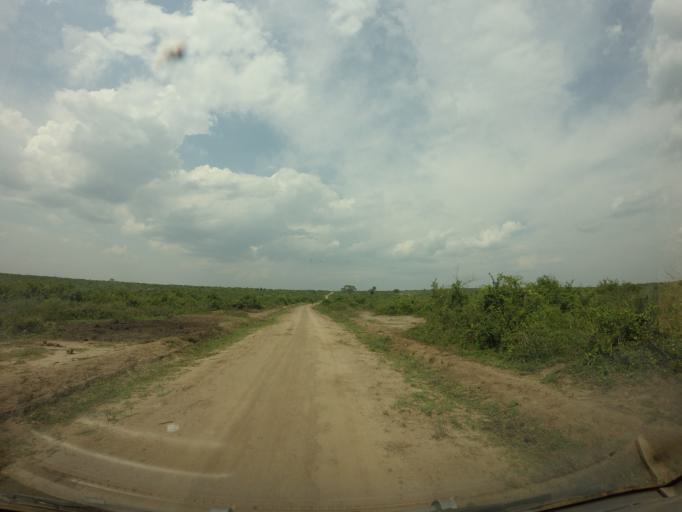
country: UG
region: Western Region
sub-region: Rubirizi District
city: Rubirizi
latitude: -0.2100
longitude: 29.9109
